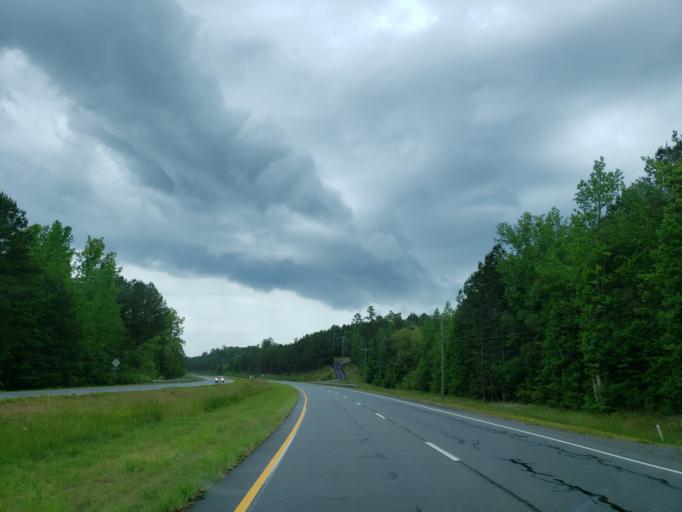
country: US
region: Georgia
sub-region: Haralson County
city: Buchanan
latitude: 33.8545
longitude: -85.2100
